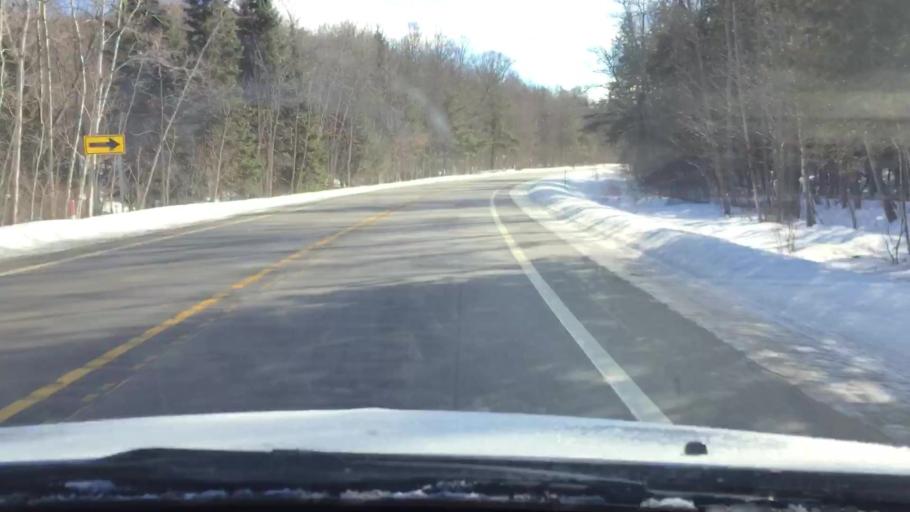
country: US
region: Michigan
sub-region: Antrim County
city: Mancelona
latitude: 45.0056
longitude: -85.0631
